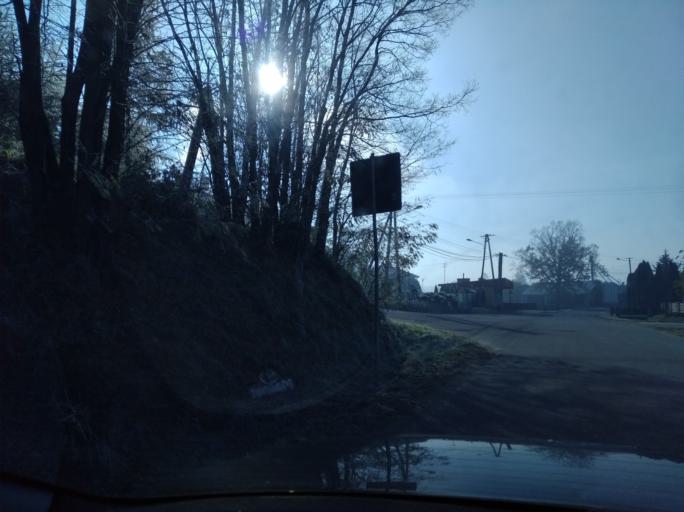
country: PL
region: Subcarpathian Voivodeship
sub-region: Powiat strzyzowski
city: Wysoka Strzyzowska
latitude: 49.8635
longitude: 21.7083
